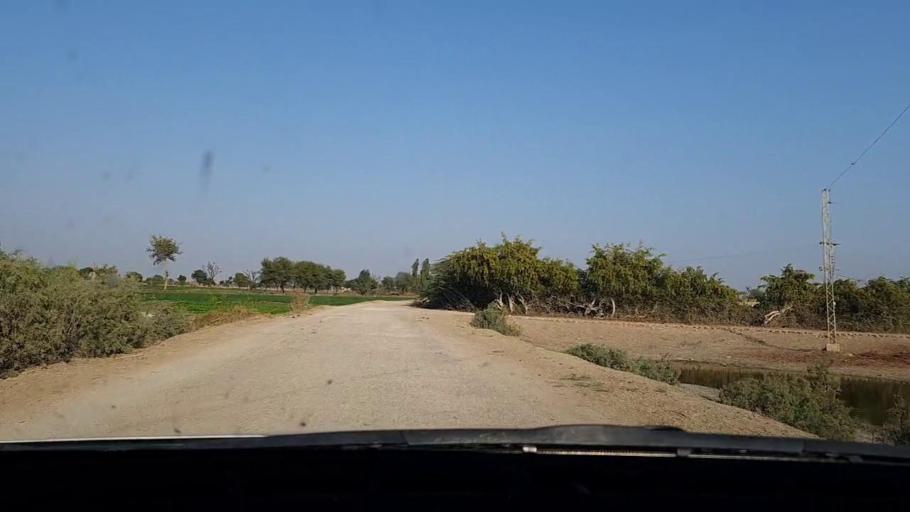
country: PK
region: Sindh
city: Tando Mittha Khan
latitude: 25.8345
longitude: 69.3293
